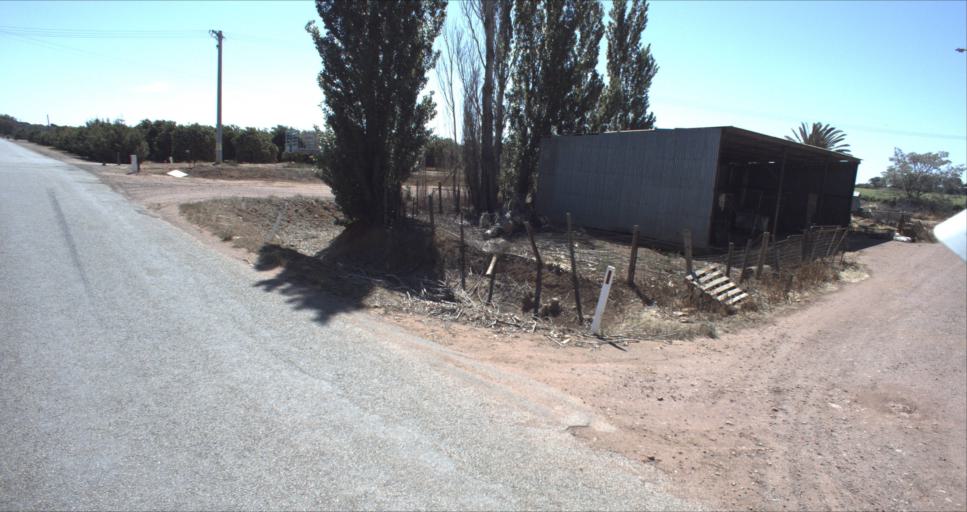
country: AU
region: New South Wales
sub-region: Leeton
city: Leeton
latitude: -34.5336
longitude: 146.3534
